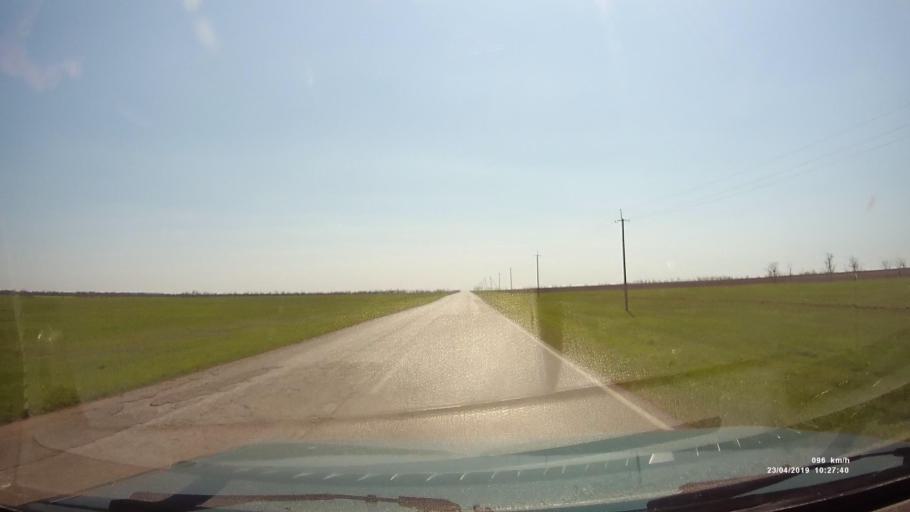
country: RU
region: Kalmykiya
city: Yashalta
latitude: 46.6119
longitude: 42.4945
